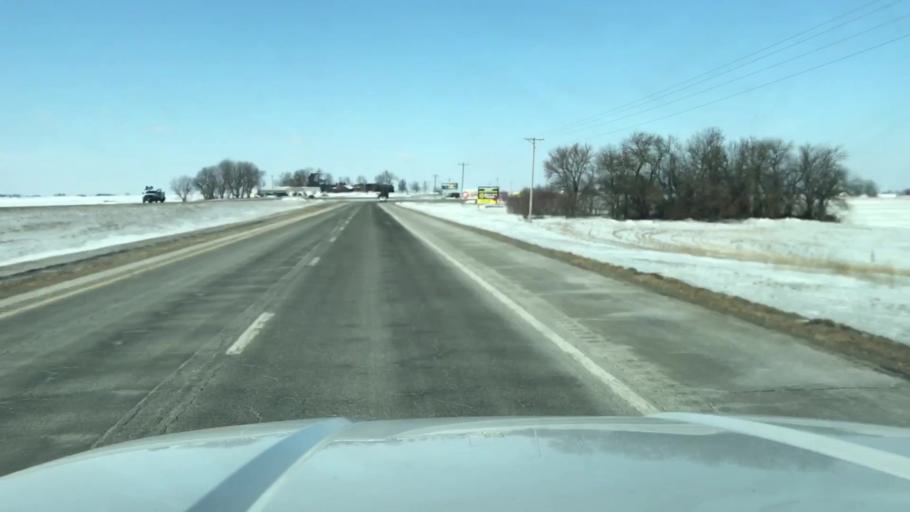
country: US
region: Missouri
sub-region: Nodaway County
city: Maryville
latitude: 40.2751
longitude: -94.8706
